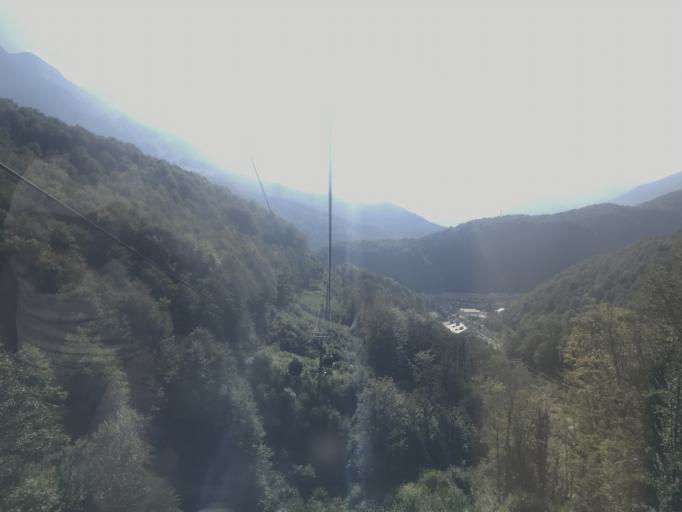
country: RU
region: Krasnodarskiy
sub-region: Sochi City
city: Krasnaya Polyana
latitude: 43.6876
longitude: 40.2930
